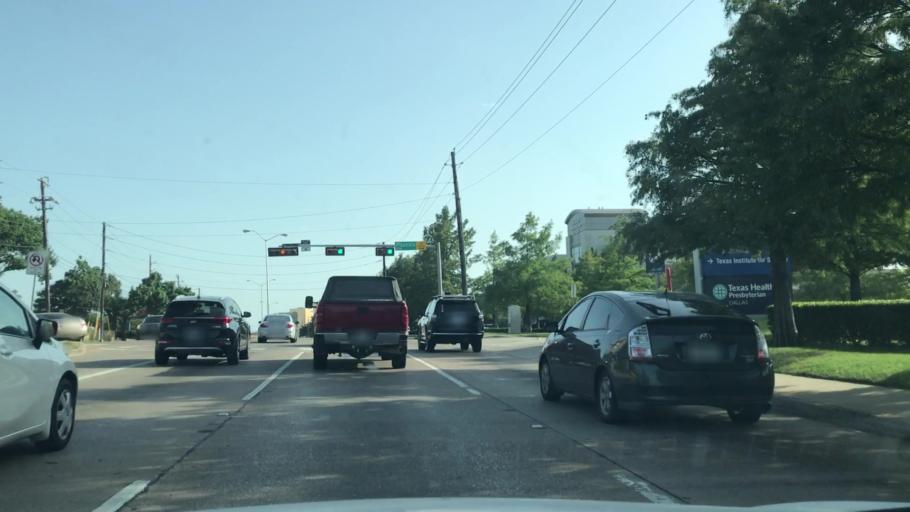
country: US
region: Texas
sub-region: Dallas County
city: University Park
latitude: 32.8779
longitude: -96.7609
